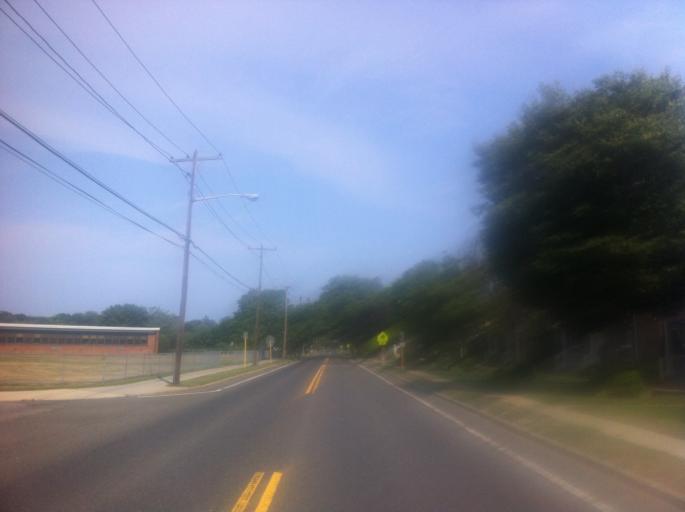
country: US
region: New York
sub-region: Suffolk County
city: Babylon
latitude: 40.7022
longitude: -73.3333
